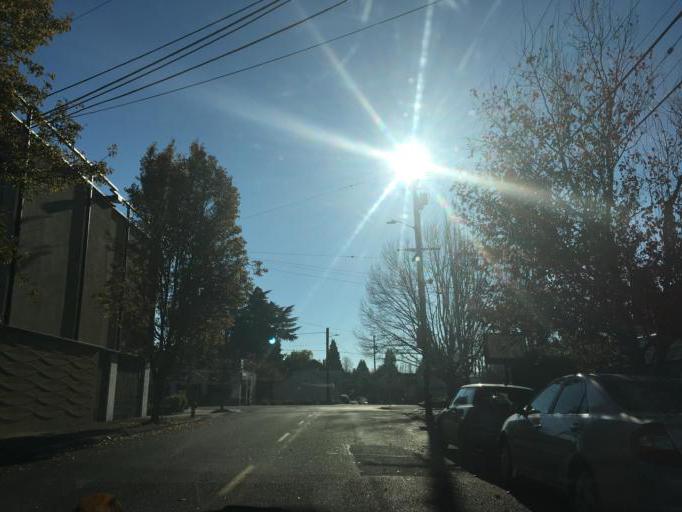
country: US
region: Oregon
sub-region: Multnomah County
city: Portland
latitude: 45.5270
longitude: -122.6444
